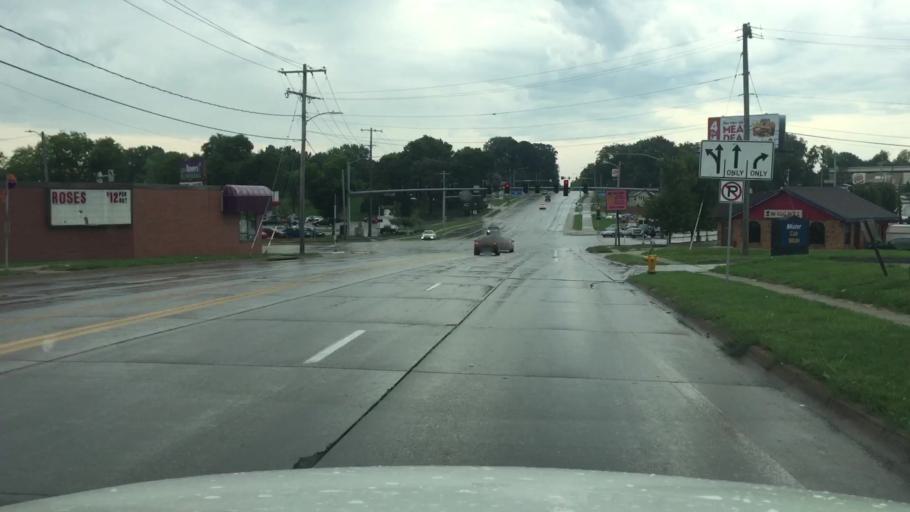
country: US
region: Iowa
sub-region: Polk County
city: Des Moines
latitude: 41.5542
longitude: -93.5978
